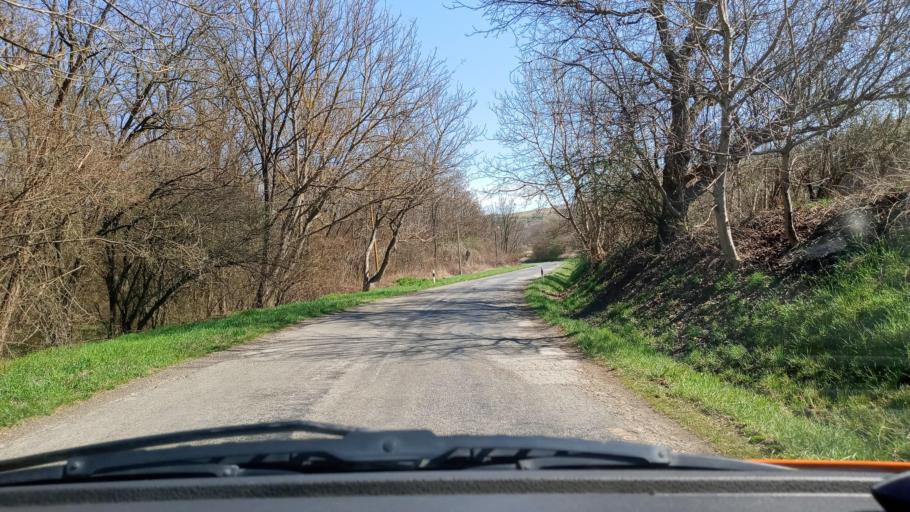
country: HU
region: Baranya
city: Boly
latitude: 46.0208
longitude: 18.4571
